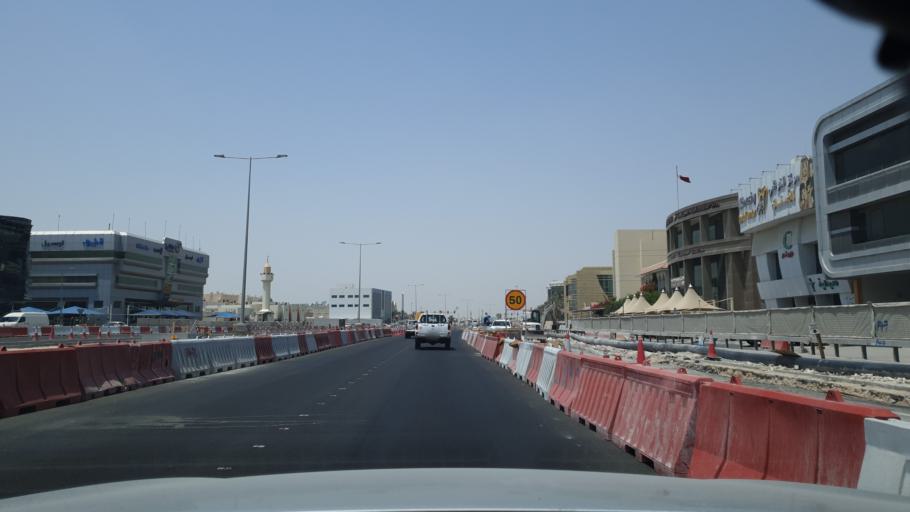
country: QA
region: Baladiyat ad Dawhah
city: Doha
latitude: 25.2561
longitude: 51.5491
